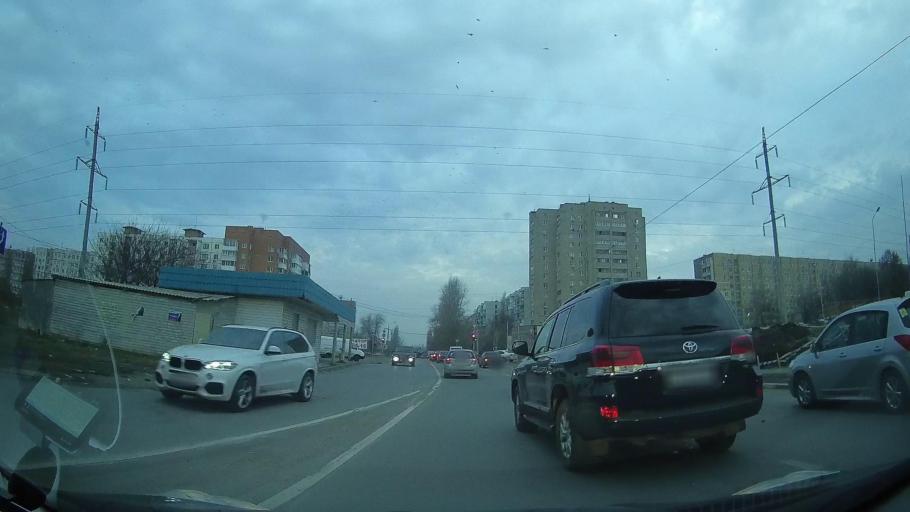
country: RU
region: Rostov
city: Severnyy
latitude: 47.3026
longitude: 39.7227
